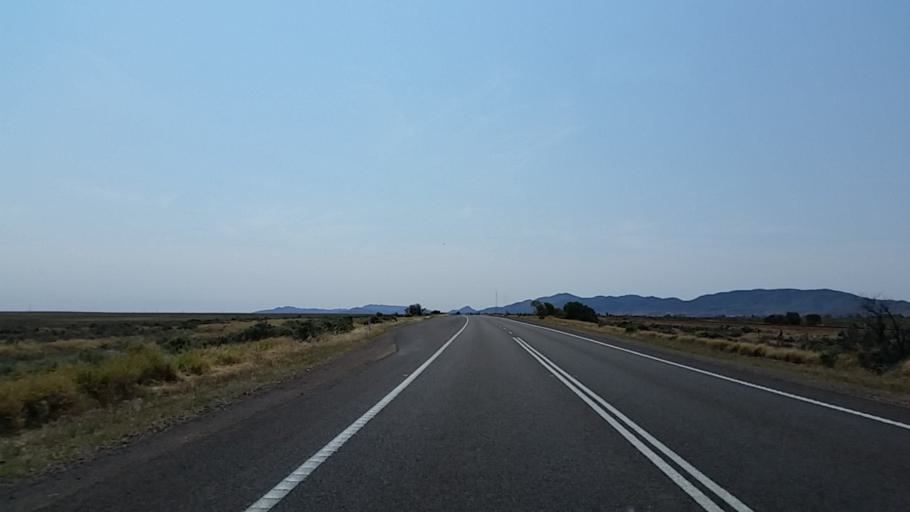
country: AU
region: South Australia
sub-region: Port Augusta
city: Port Augusta
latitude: -32.7080
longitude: 137.9416
